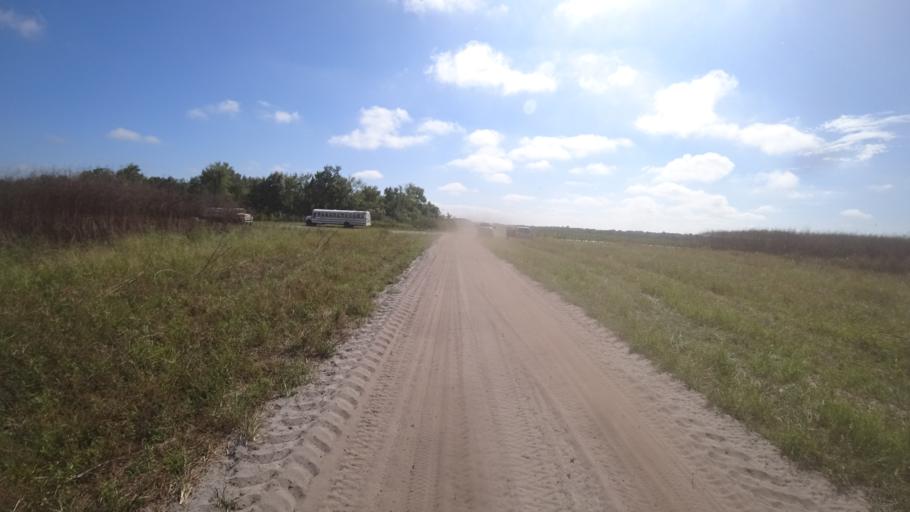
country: US
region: Florida
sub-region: DeSoto County
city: Arcadia
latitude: 27.2872
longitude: -82.0789
